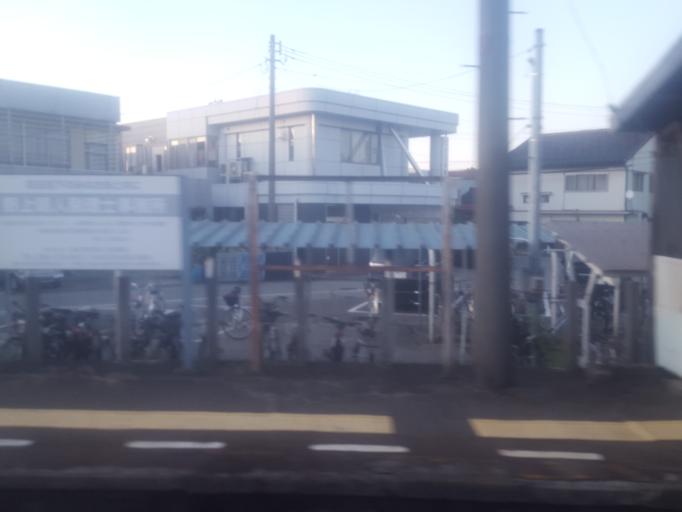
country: JP
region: Toyama
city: Toyama-shi
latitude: 36.6988
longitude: 137.2534
